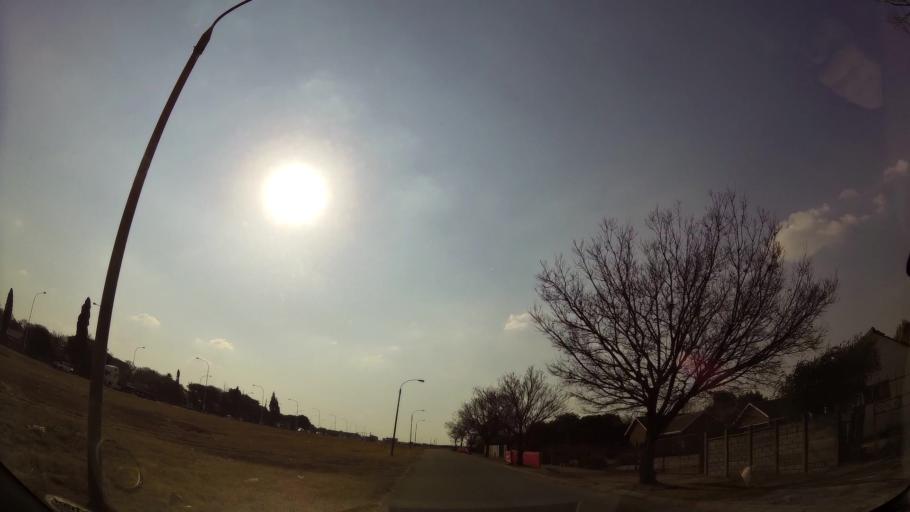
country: ZA
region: Gauteng
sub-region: Ekurhuleni Metropolitan Municipality
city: Benoni
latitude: -26.1631
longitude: 28.2787
